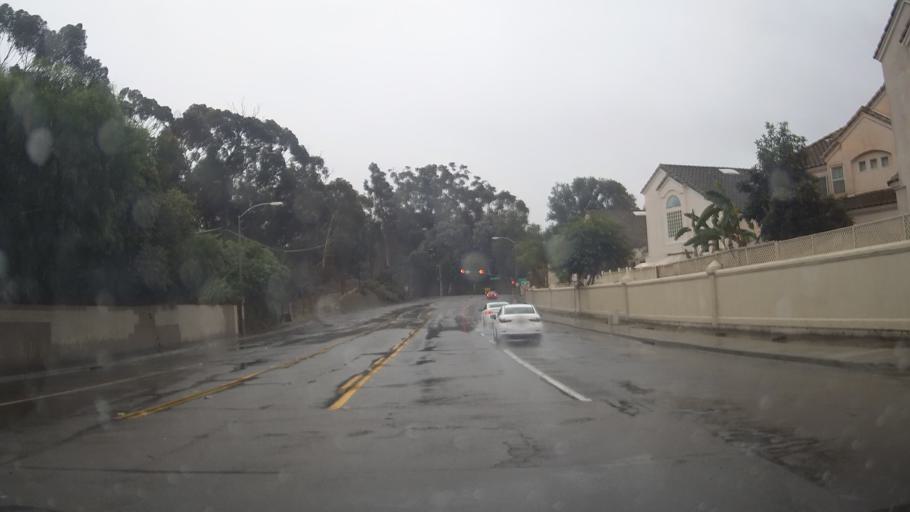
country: US
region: California
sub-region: San Diego County
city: Bonita
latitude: 32.6610
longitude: -117.0561
